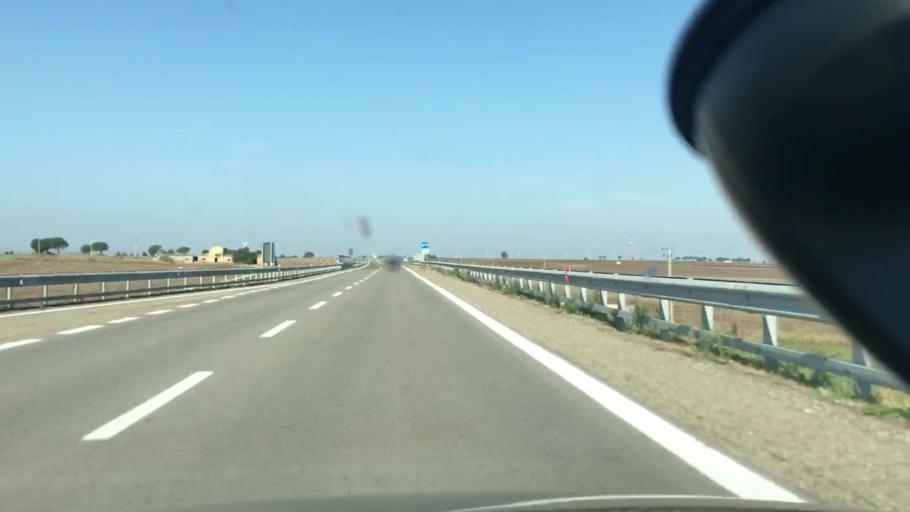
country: IT
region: Basilicate
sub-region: Provincia di Potenza
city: Montemilone
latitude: 40.9869
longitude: 15.9118
